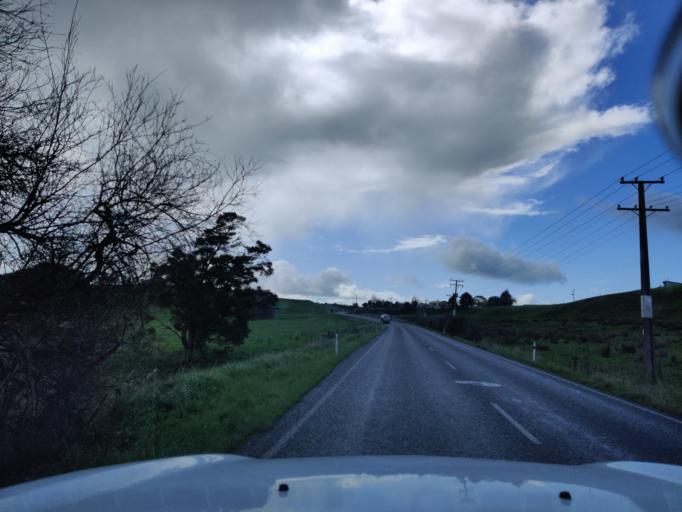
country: NZ
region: Waikato
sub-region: Waikato District
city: Ngaruawahia
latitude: -37.5789
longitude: 175.2254
